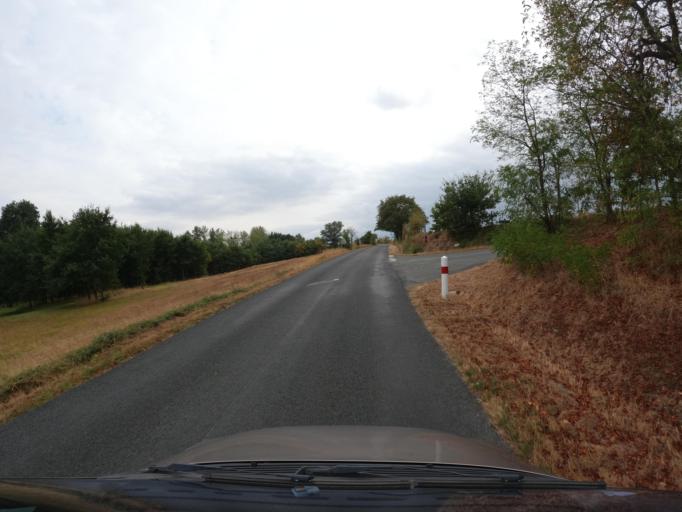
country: FR
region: Pays de la Loire
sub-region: Departement de la Vendee
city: Tiffauges
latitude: 46.9918
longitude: -1.1085
